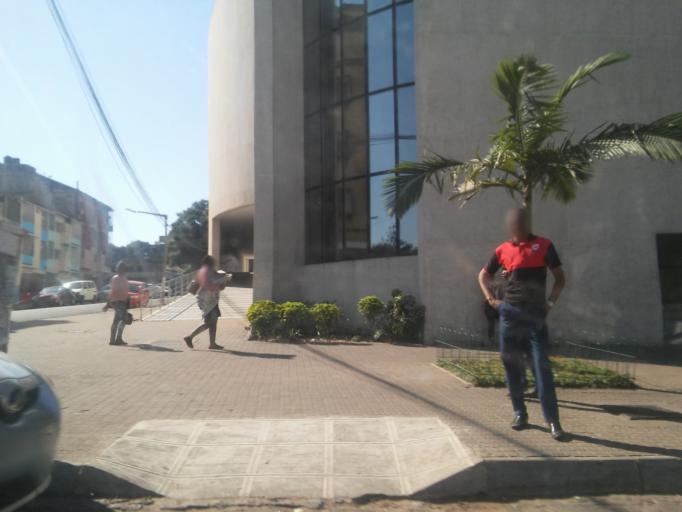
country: MZ
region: Maputo City
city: Maputo
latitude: -25.9614
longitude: 32.5665
